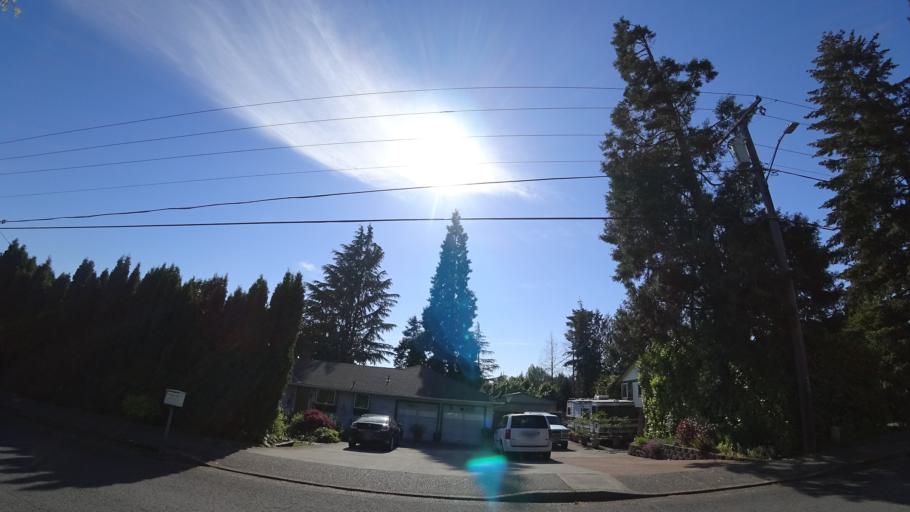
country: US
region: Oregon
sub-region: Washington County
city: Beaverton
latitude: 45.4572
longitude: -122.8080
